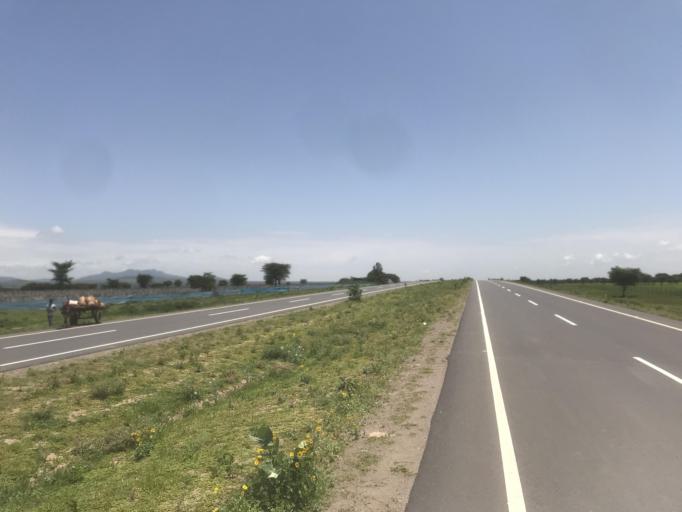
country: ET
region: Oromiya
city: Mojo
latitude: 8.3643
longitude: 38.9924
